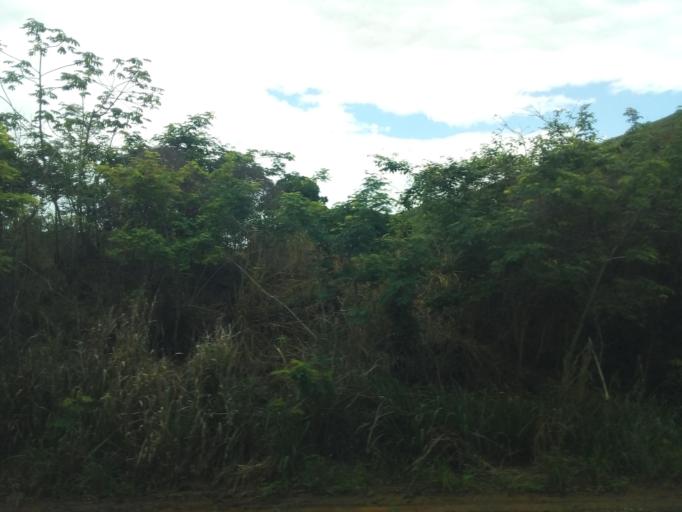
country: BR
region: Minas Gerais
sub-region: Governador Valadares
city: Governador Valadares
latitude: -19.0787
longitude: -42.1593
